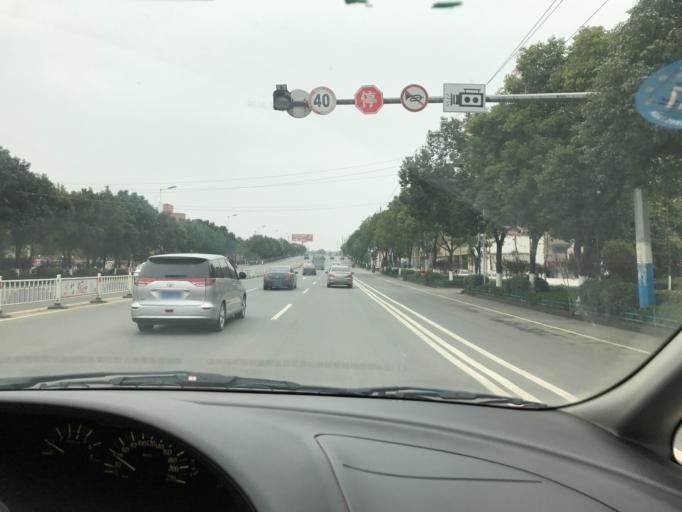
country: CN
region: Hubei
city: Anlu
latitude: 31.2511
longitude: 113.6968
